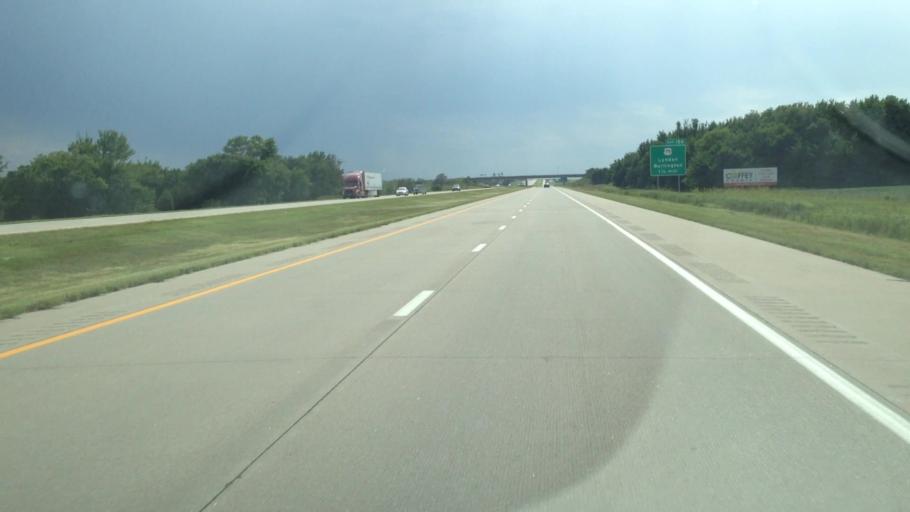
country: US
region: Kansas
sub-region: Osage County
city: Lyndon
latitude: 38.4360
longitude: -95.7031
